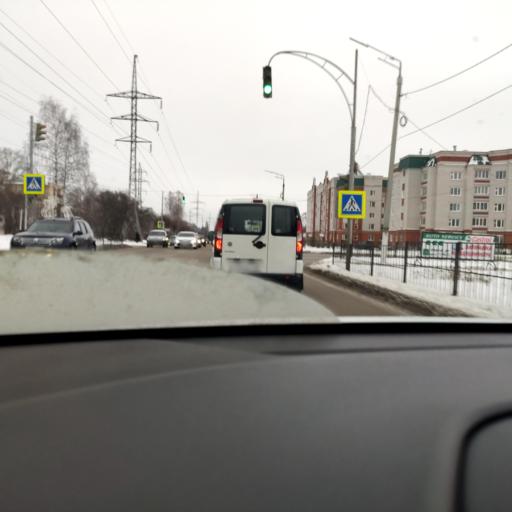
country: RU
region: Tatarstan
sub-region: Zelenodol'skiy Rayon
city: Zelenodolsk
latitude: 55.8530
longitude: 48.5012
